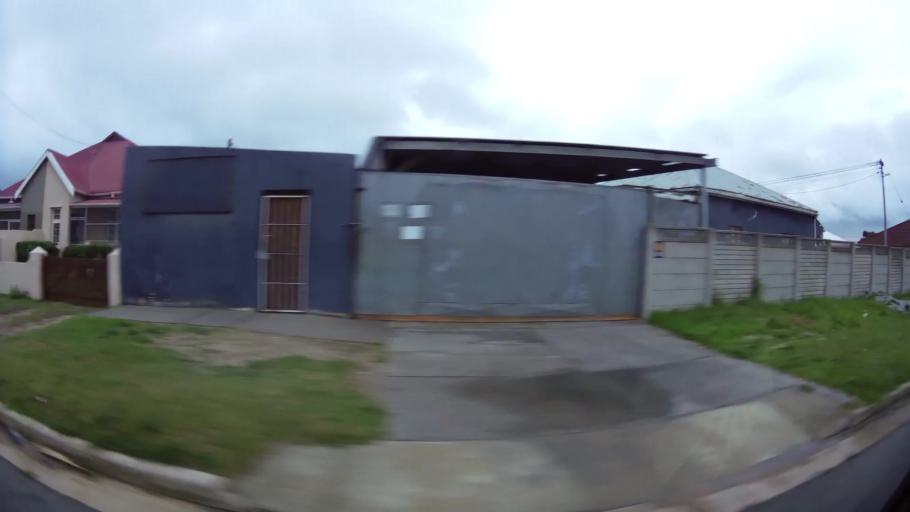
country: ZA
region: Eastern Cape
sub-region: Nelson Mandela Bay Metropolitan Municipality
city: Port Elizabeth
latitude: -33.9304
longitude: 25.5985
